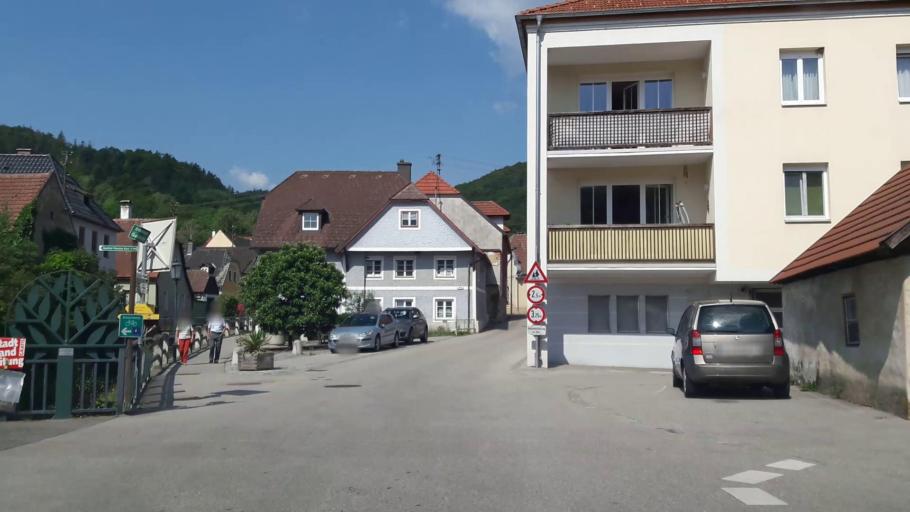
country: AT
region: Lower Austria
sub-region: Politischer Bezirk Krems
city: Aggsbach
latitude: 48.2940
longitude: 15.4039
